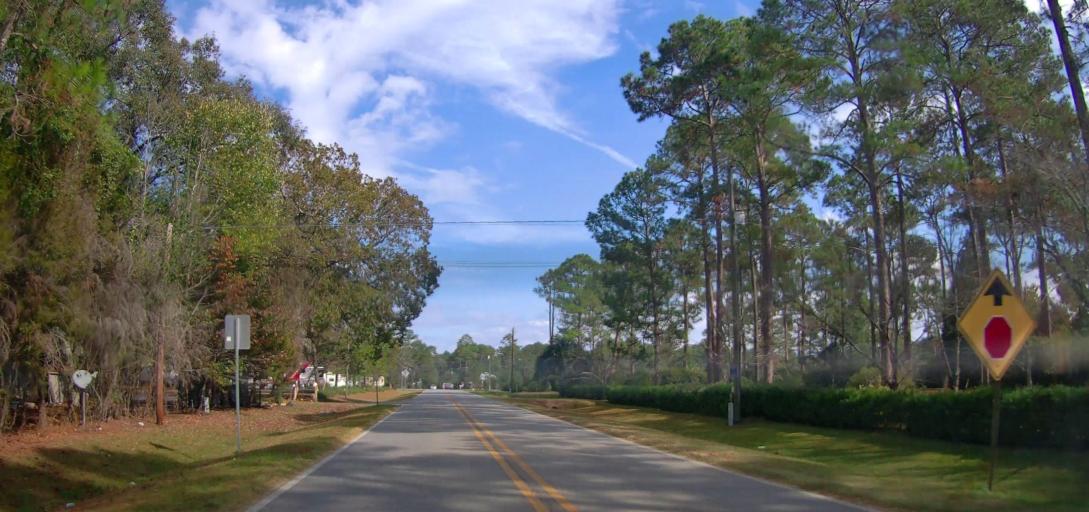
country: US
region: Georgia
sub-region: Thomas County
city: Thomasville
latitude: 30.9496
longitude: -84.0264
